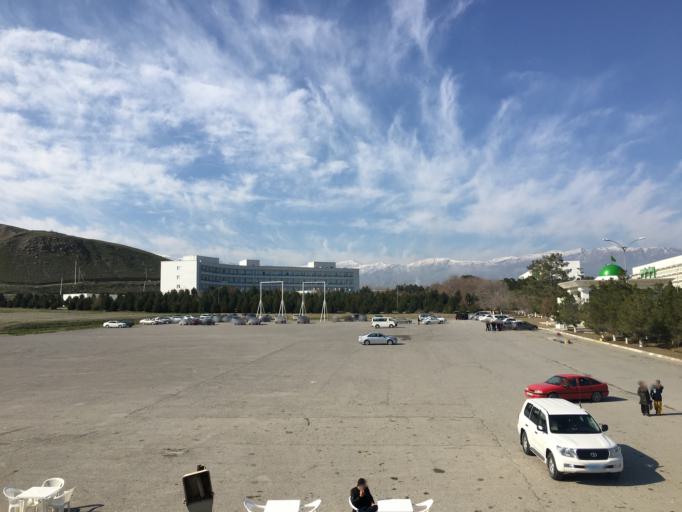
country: TM
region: Ahal
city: Baharly
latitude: 38.5172
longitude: 57.1793
